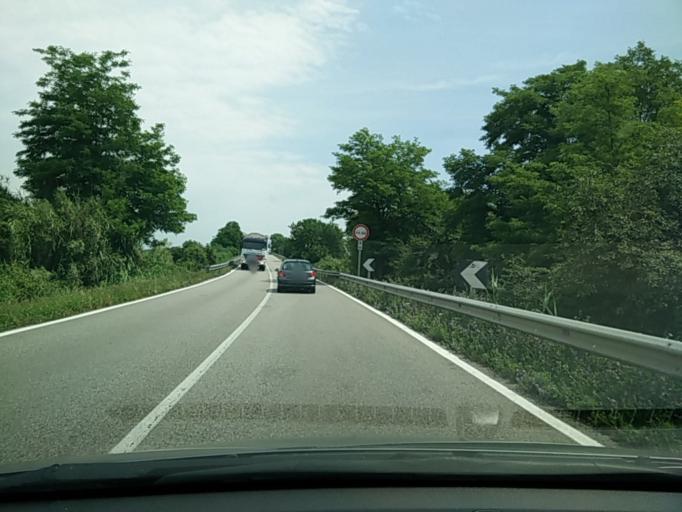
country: IT
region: Veneto
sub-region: Provincia di Venezia
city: San Liberale
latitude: 45.5287
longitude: 12.3867
